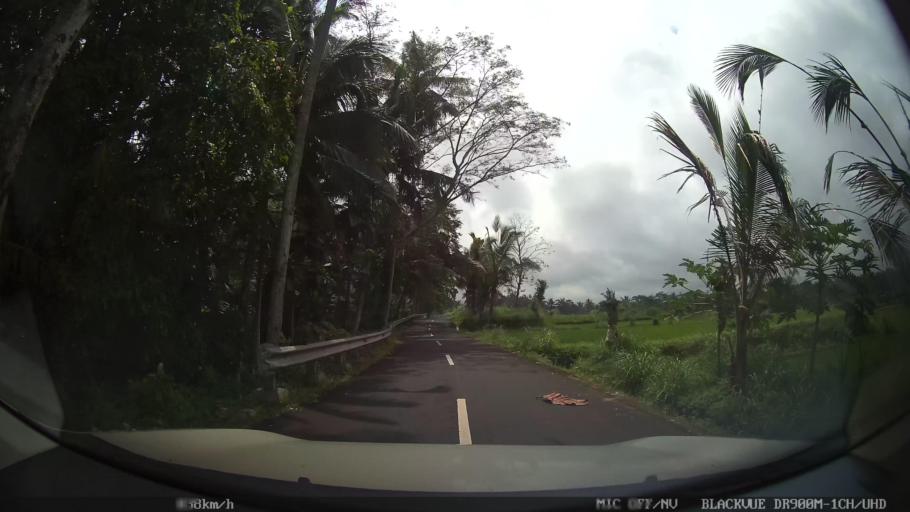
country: ID
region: Bali
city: Bayad
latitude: -8.4594
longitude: 115.2329
